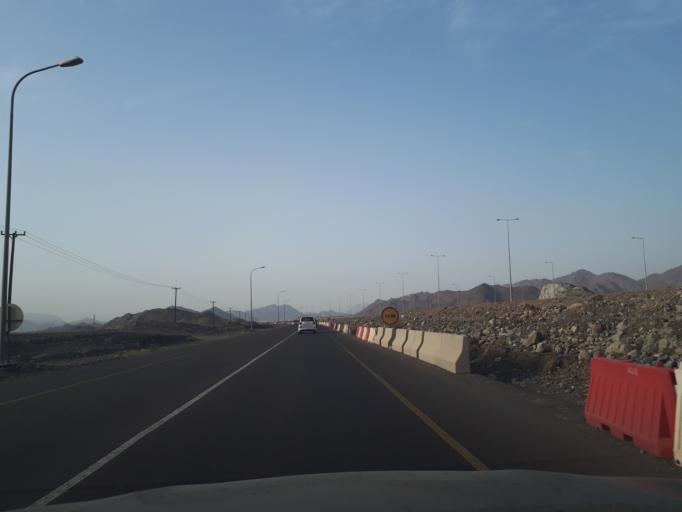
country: OM
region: Muhafazat ad Dakhiliyah
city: Sufalat Sama'il
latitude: 23.2760
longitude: 58.1061
